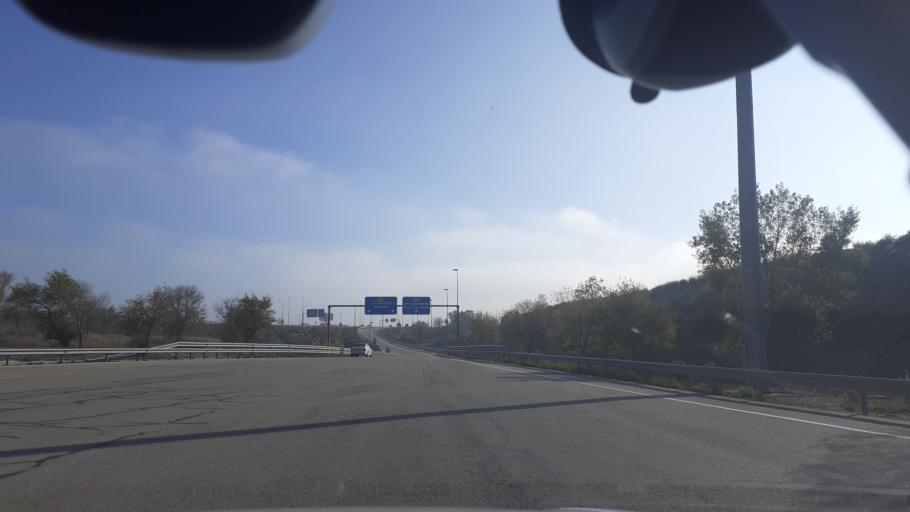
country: ES
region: Madrid
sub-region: Provincia de Madrid
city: Vicalvaro
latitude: 40.4022
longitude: -3.5769
